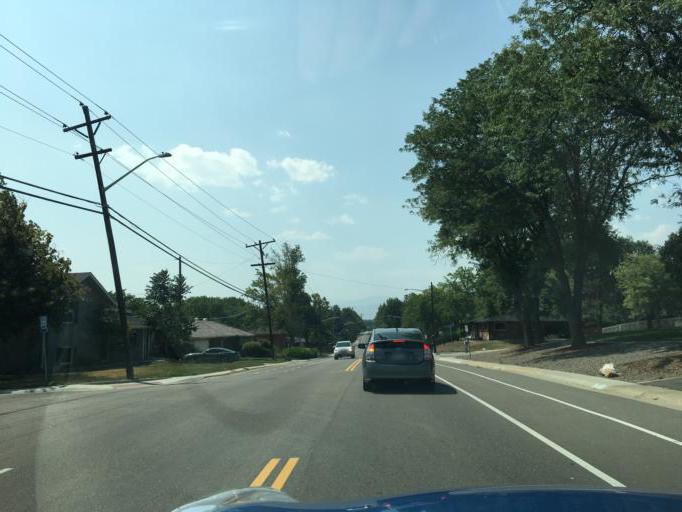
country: US
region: Colorado
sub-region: Jefferson County
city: Arvada
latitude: 39.8129
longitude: -105.0829
